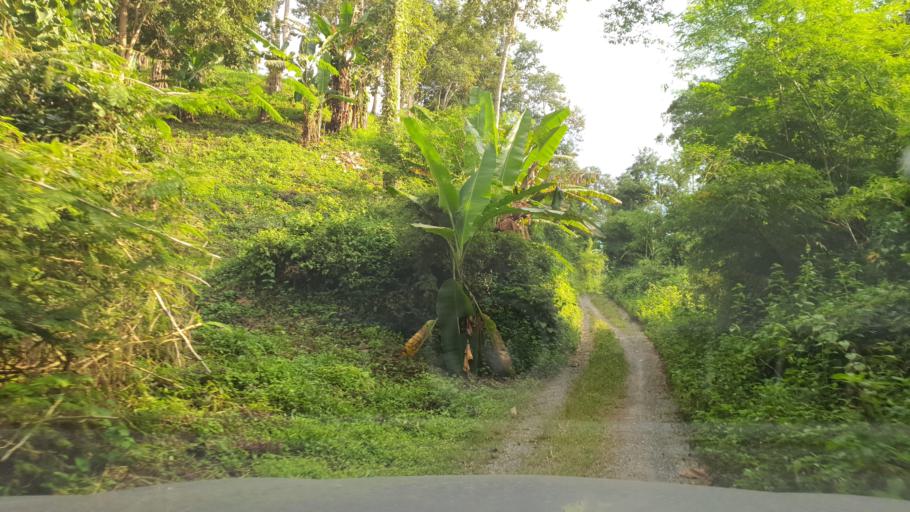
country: TH
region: Chiang Mai
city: Mae On
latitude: 18.8857
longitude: 99.2669
